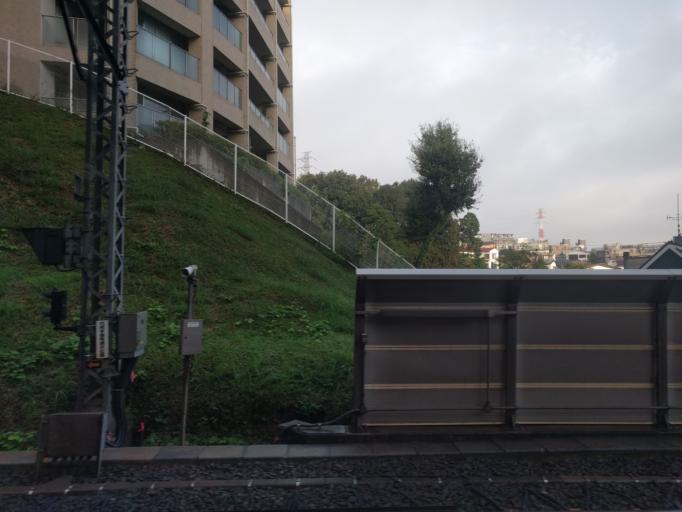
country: JP
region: Tokyo
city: Chofugaoka
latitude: 35.5968
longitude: 139.6075
